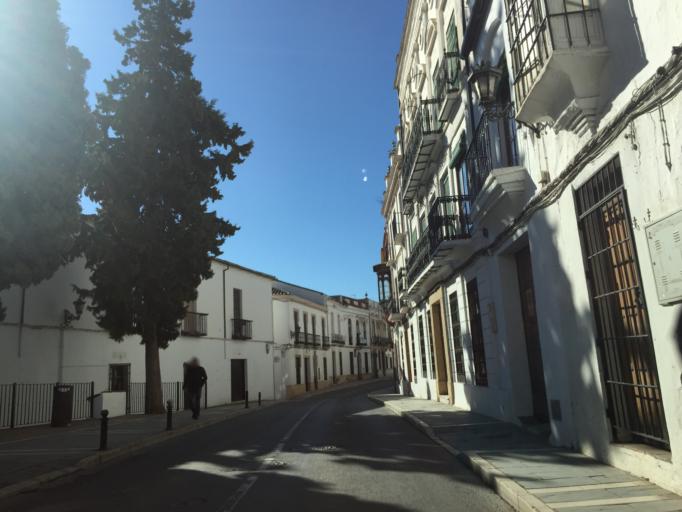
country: ES
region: Andalusia
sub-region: Provincia de Malaga
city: Ronda
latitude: 36.7394
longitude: -5.1653
